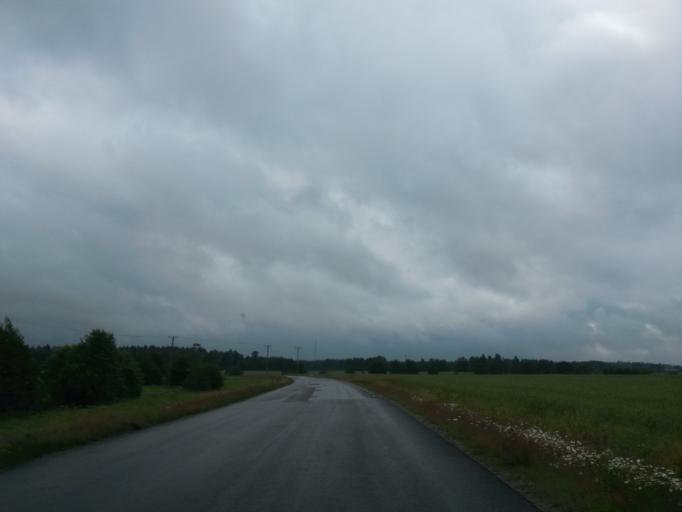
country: SE
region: Vaestra Goetaland
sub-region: Essunga Kommun
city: Nossebro
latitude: 58.1618
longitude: 12.7453
